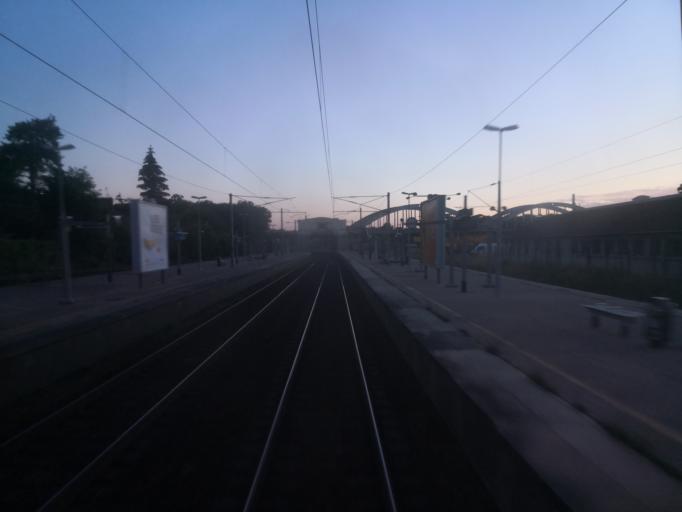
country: FR
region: Ile-de-France
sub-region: Departement des Yvelines
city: Acheres
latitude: 48.9556
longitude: 2.0946
